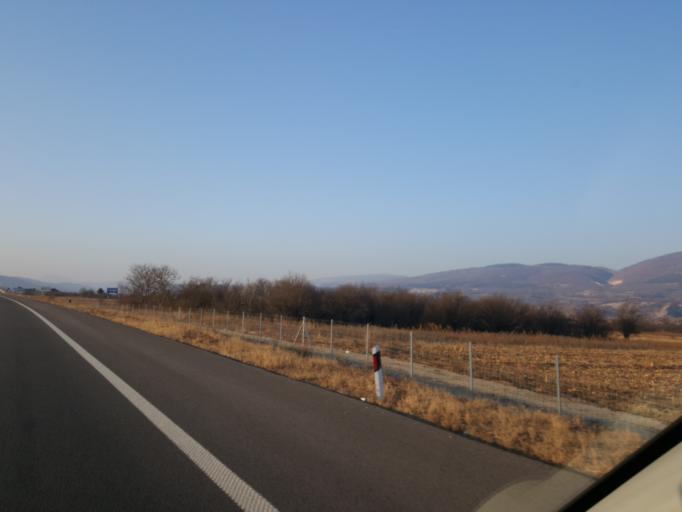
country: RS
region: Central Serbia
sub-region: Pirotski Okrug
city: Pirot
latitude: 43.1157
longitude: 22.6273
